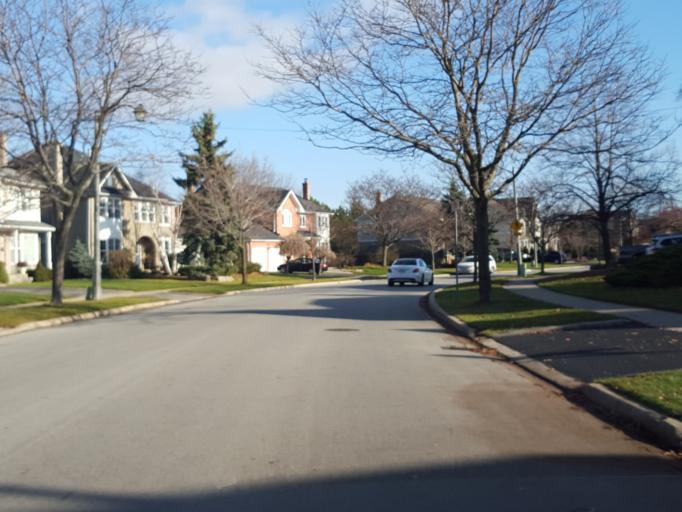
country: CA
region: Ontario
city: Burlington
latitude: 43.3908
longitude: -79.8025
